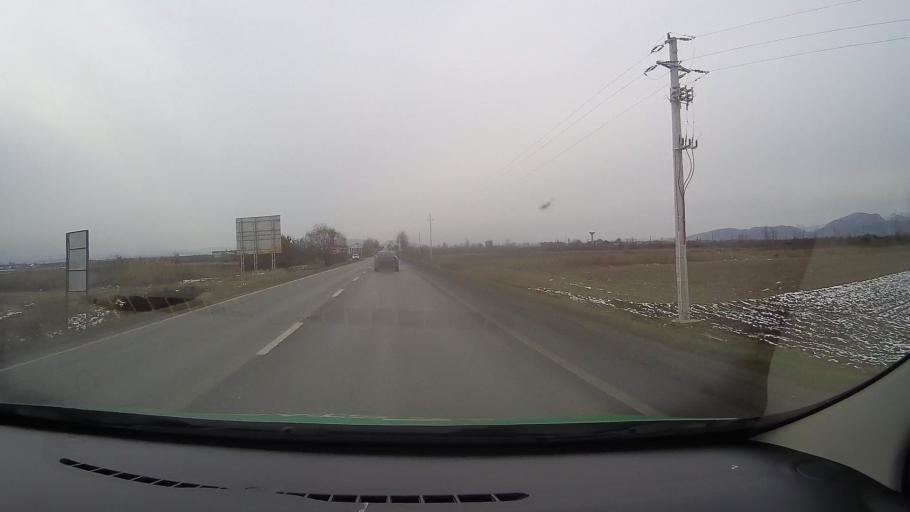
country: RO
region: Hunedoara
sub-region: Oras Simeria
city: Simeria
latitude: 45.8361
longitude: 23.0331
